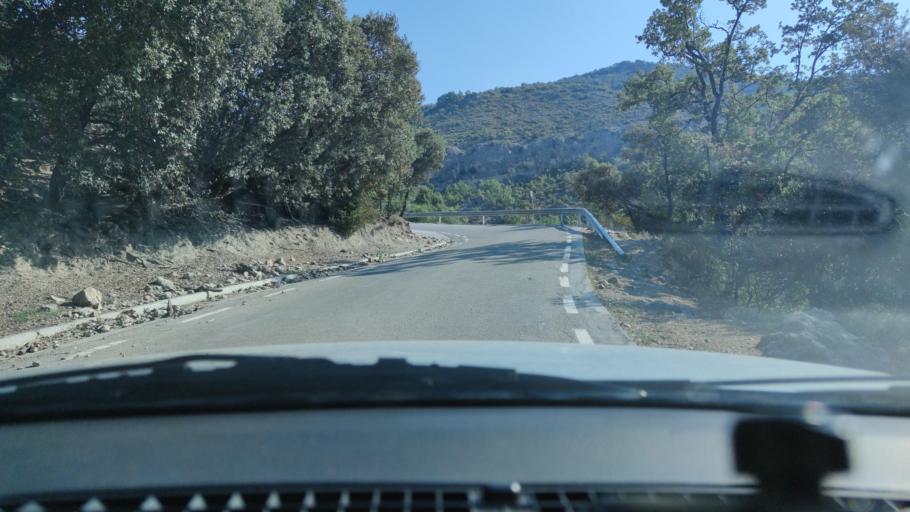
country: ES
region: Catalonia
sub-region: Provincia de Lleida
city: Llimiana
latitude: 42.0849
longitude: 0.8425
